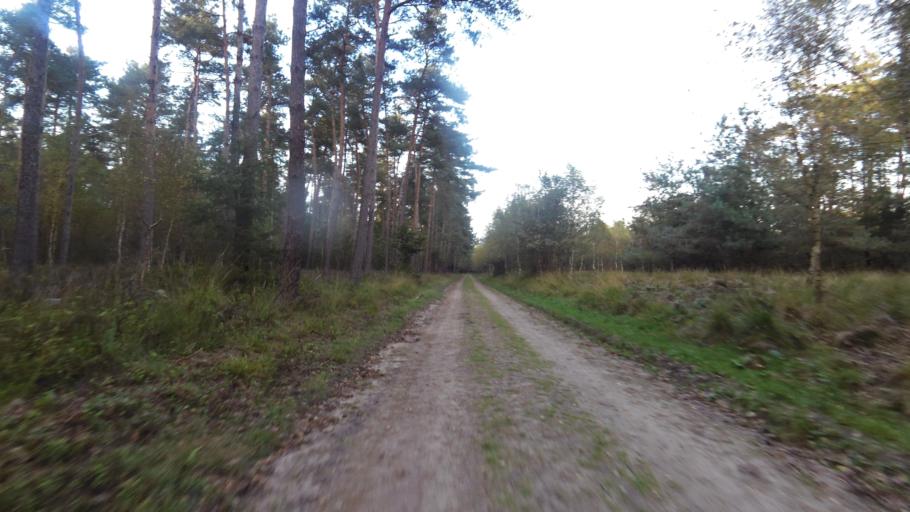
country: NL
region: Gelderland
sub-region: Gemeente Nunspeet
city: Nunspeet
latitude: 52.3212
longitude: 5.8396
